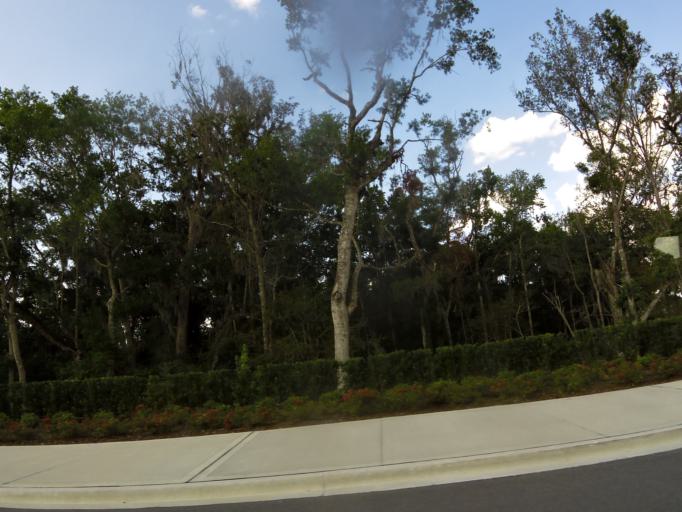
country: US
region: Florida
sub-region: Clay County
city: Green Cove Springs
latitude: 30.0201
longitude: -81.6340
